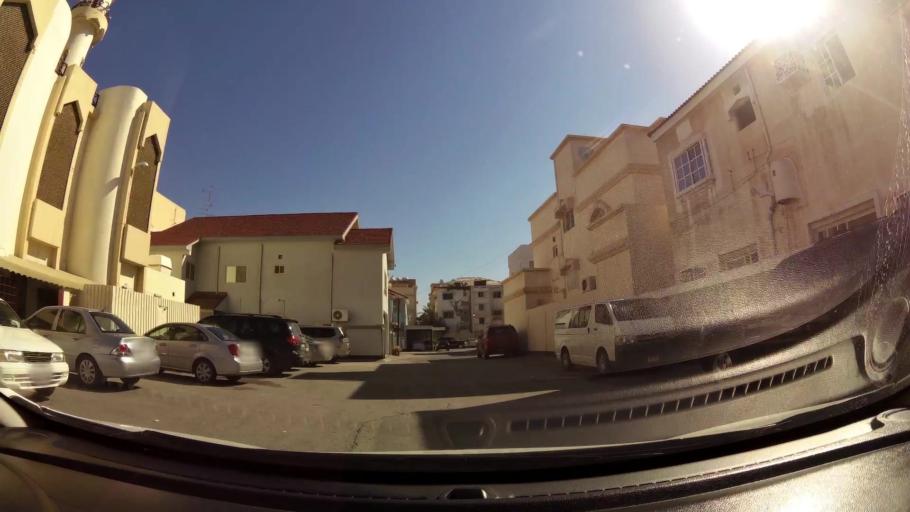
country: BH
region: Muharraq
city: Al Muharraq
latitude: 26.2647
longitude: 50.6189
